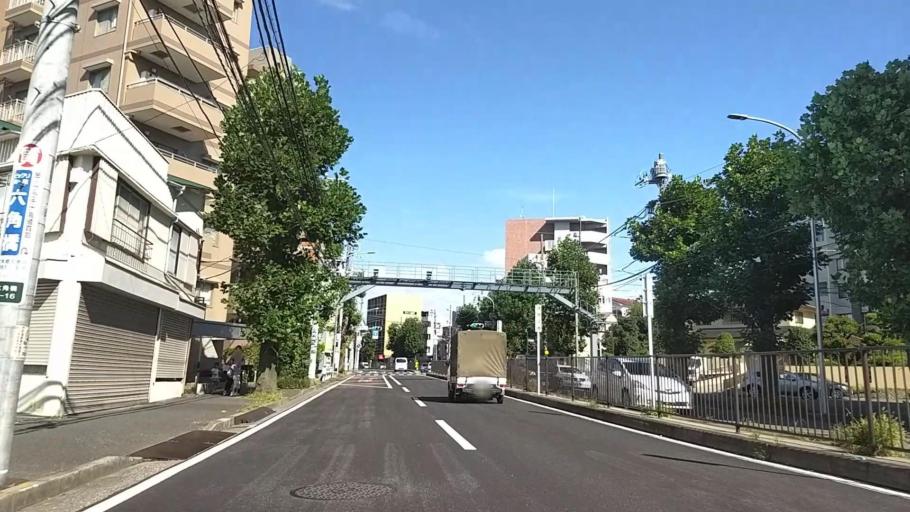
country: JP
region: Kanagawa
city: Yokohama
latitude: 35.4885
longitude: 139.6241
